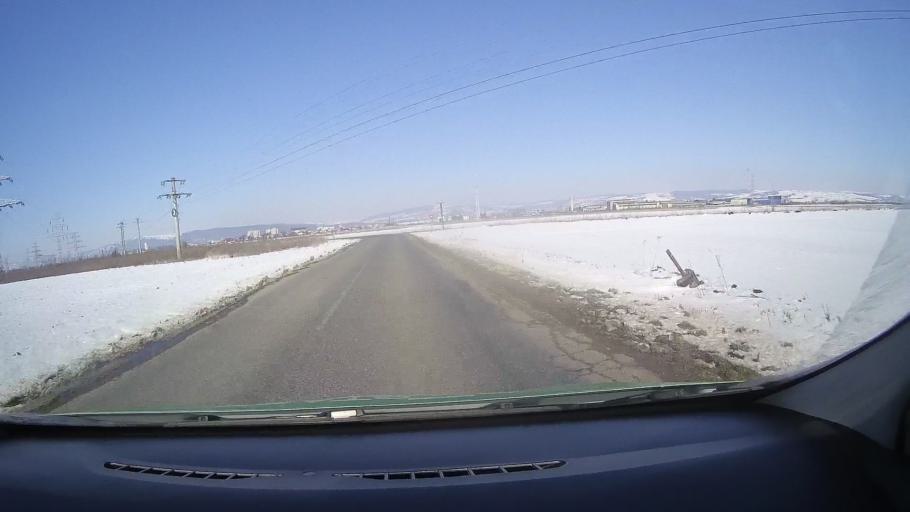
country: RO
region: Brasov
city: Fogarasch
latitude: 45.8172
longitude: 24.9872
